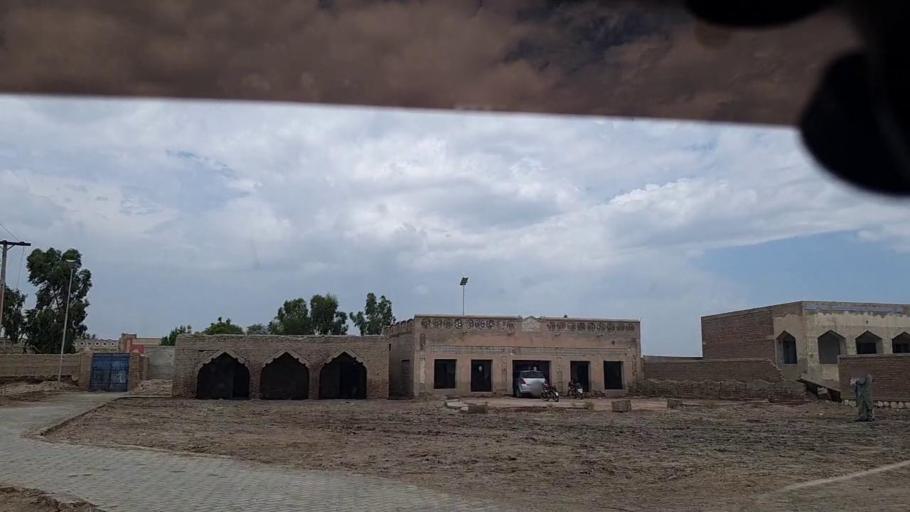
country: PK
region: Sindh
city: Ghauspur
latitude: 28.1161
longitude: 68.9885
